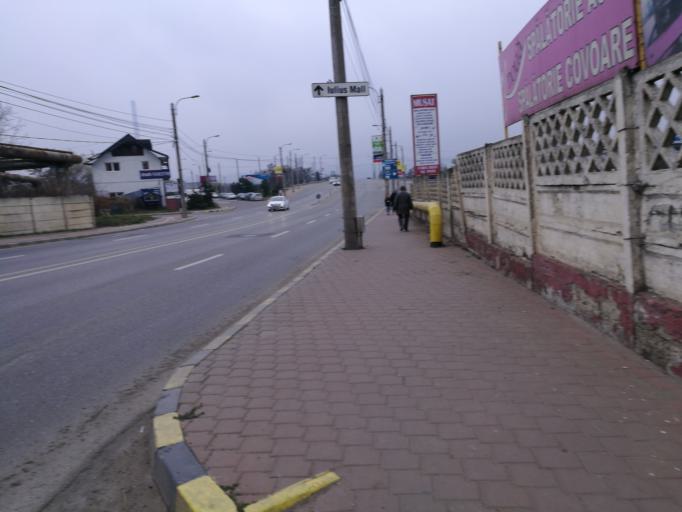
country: RO
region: Suceava
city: Suceava
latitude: 47.6694
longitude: 26.2749
